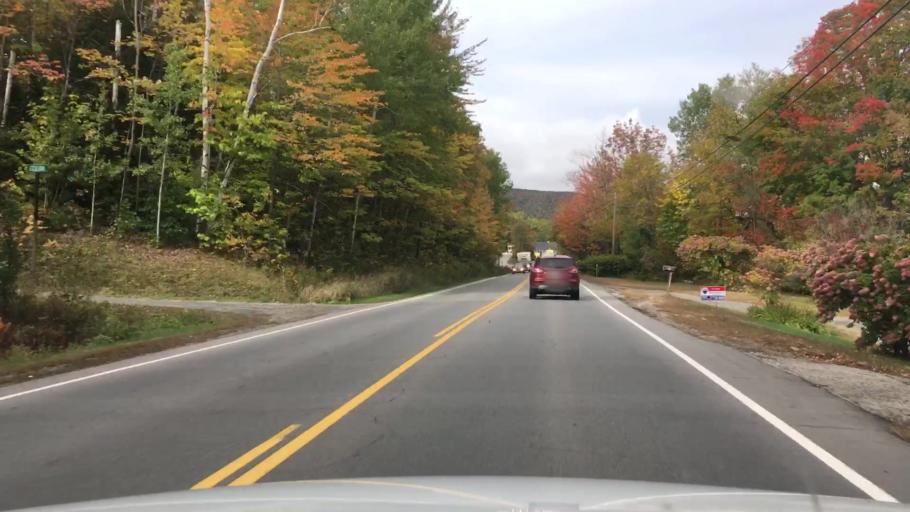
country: US
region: New Hampshire
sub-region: Coos County
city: Gorham
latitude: 44.3854
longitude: -71.1530
